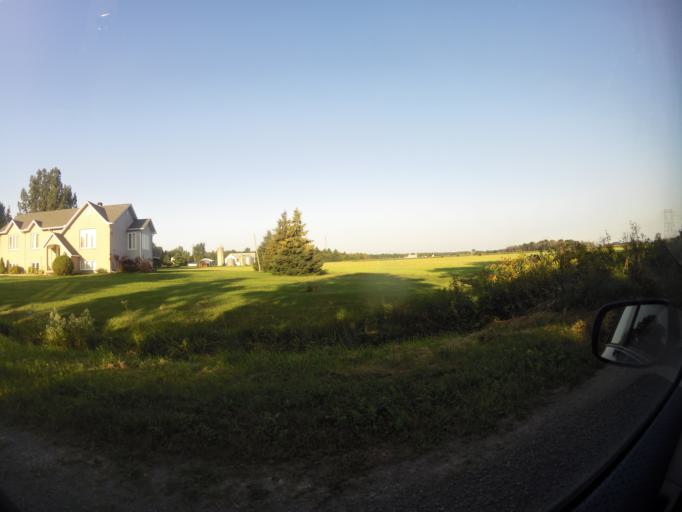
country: CA
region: Ontario
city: Clarence-Rockland
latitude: 45.4978
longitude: -75.4127
